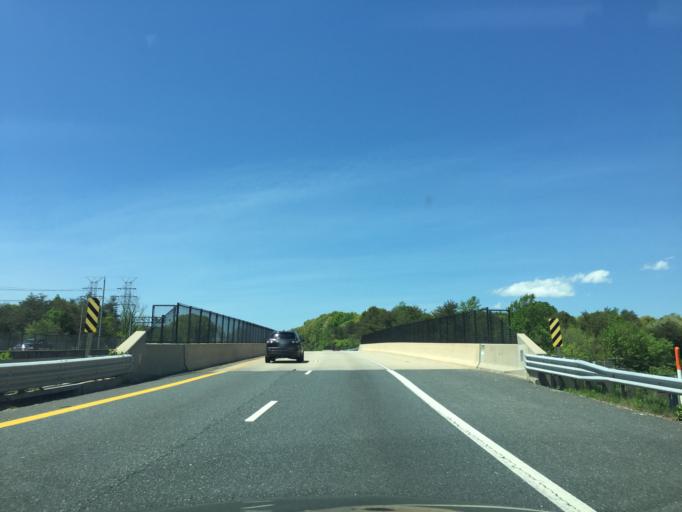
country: US
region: Maryland
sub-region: Baltimore County
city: White Marsh
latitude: 39.3739
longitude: -76.4319
